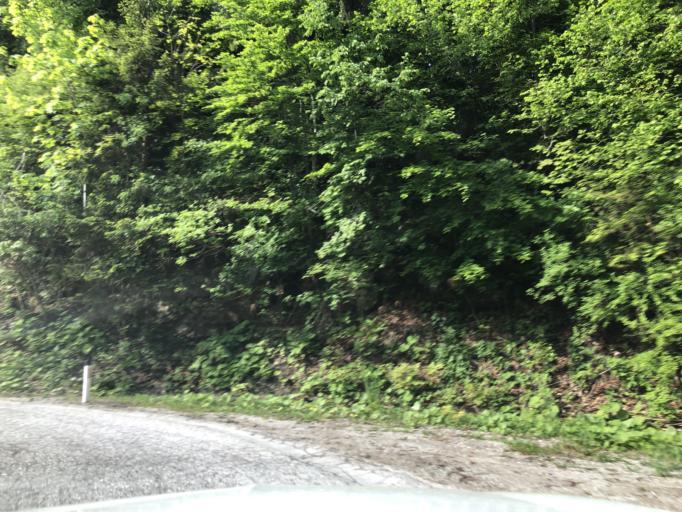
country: SI
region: Bloke
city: Nova Vas
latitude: 45.8003
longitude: 14.5549
